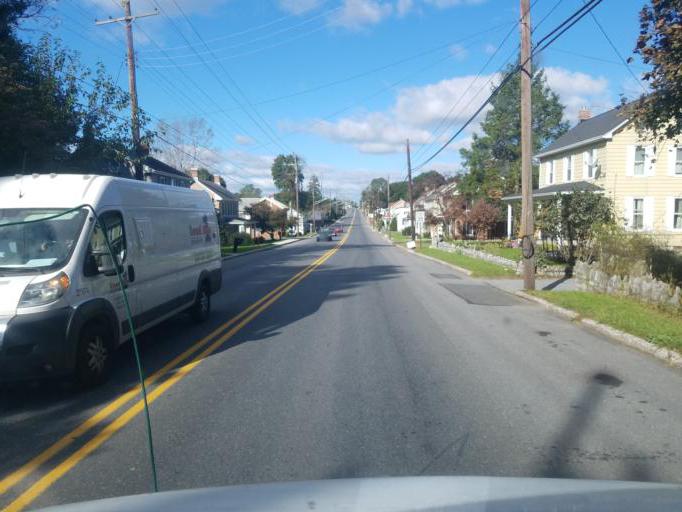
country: US
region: Pennsylvania
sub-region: Franklin County
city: Greencastle
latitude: 39.7782
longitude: -77.6709
